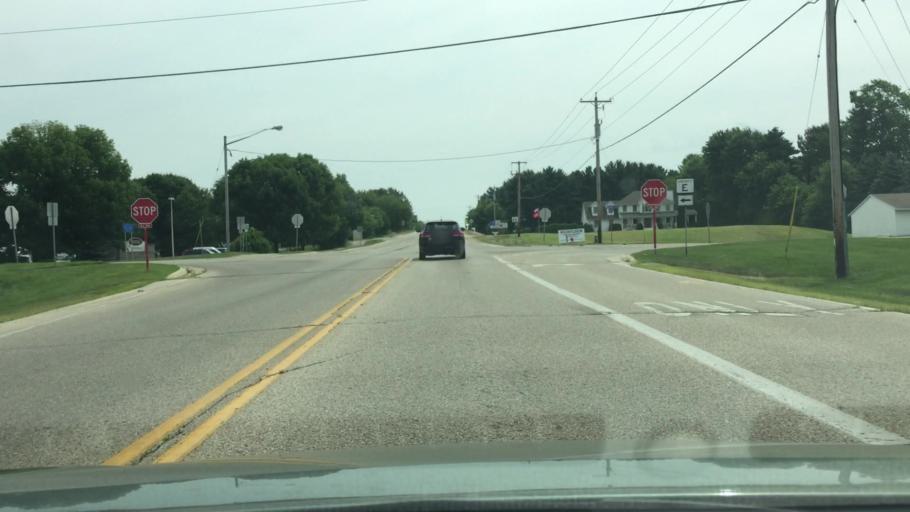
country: US
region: Wisconsin
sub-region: Waukesha County
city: Hartland
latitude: 43.0830
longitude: -88.3442
